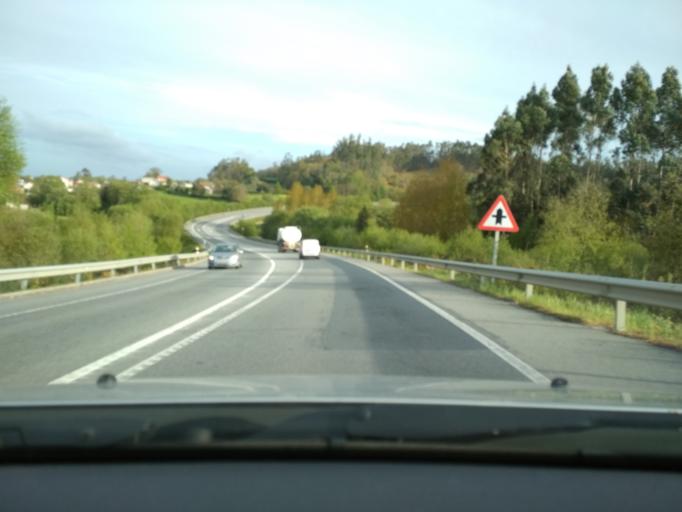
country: ES
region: Galicia
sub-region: Provincia da Coruna
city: Cerceda
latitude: 43.2197
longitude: -8.4580
